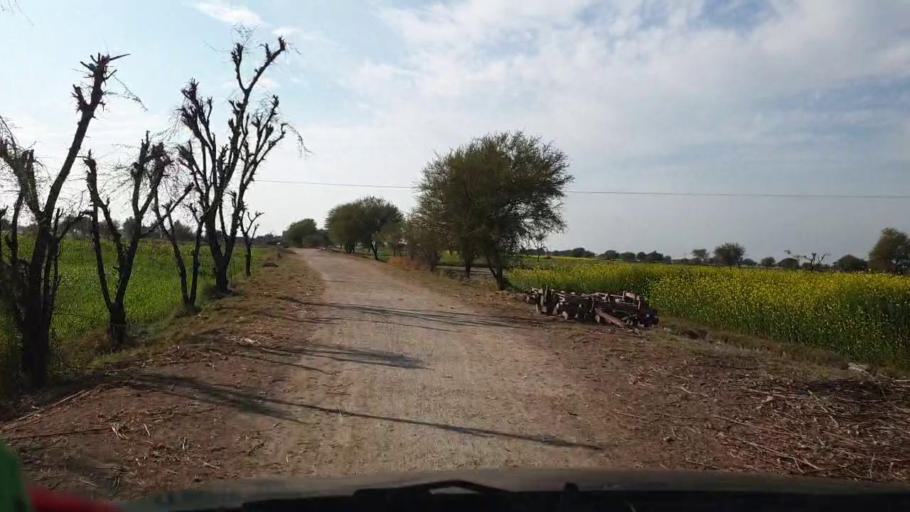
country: PK
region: Sindh
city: Sinjhoro
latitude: 25.9826
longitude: 68.8389
